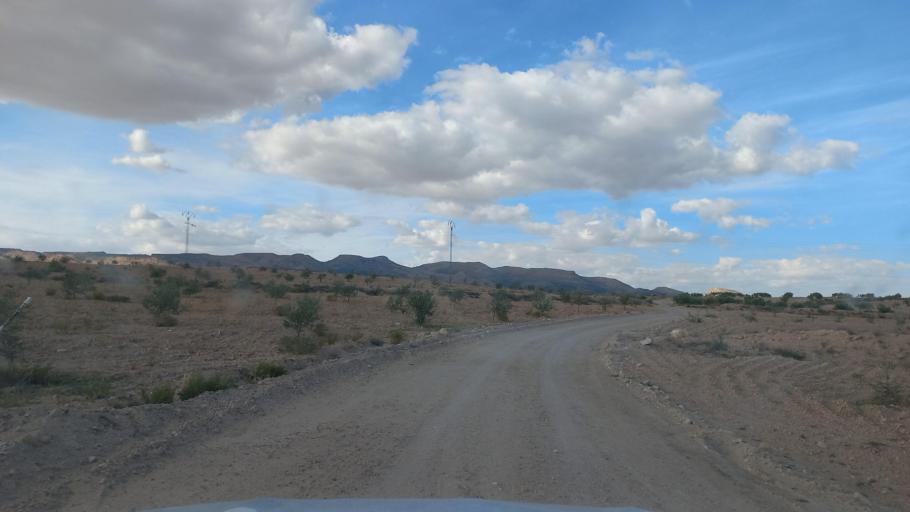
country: TN
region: Al Qasrayn
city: Sbiba
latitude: 35.3950
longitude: 9.0145
